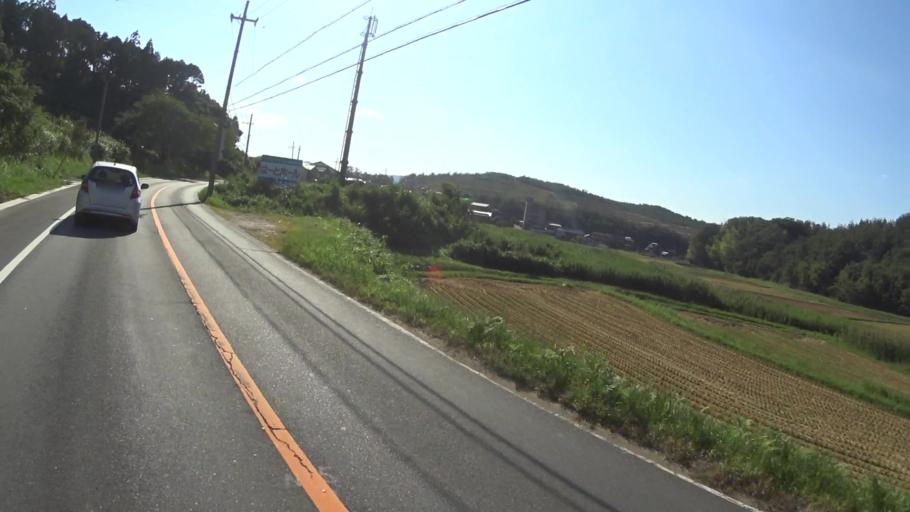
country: JP
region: Kyoto
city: Miyazu
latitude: 35.6986
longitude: 135.0596
